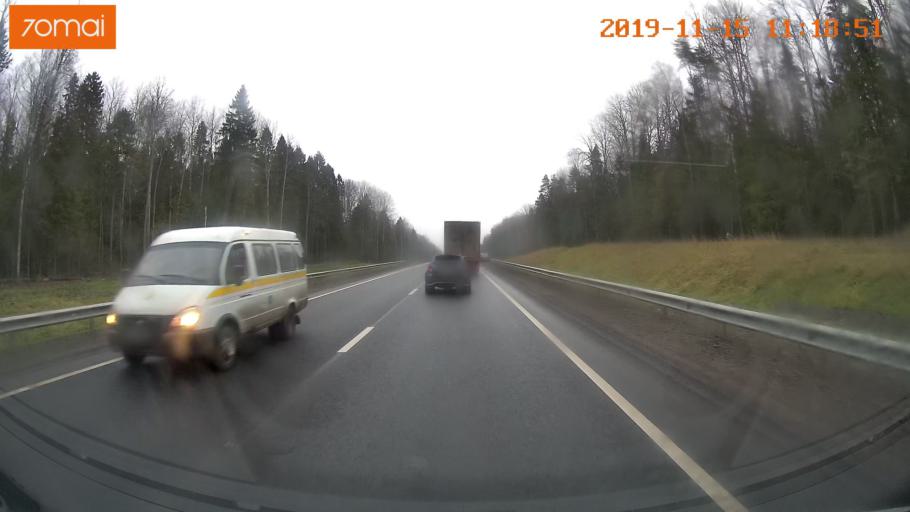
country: RU
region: Vologda
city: Molochnoye
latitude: 59.1370
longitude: 39.2805
